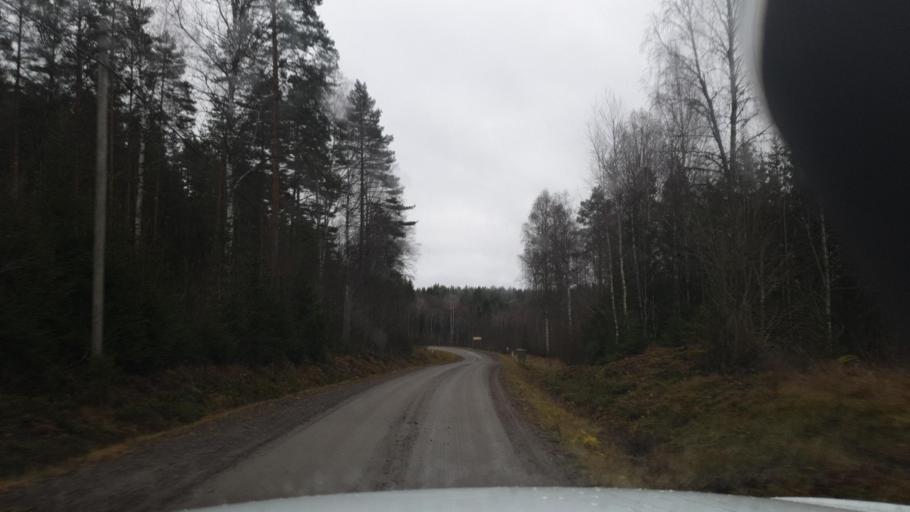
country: SE
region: Vaermland
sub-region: Eda Kommun
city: Charlottenberg
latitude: 59.9309
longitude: 12.3729
